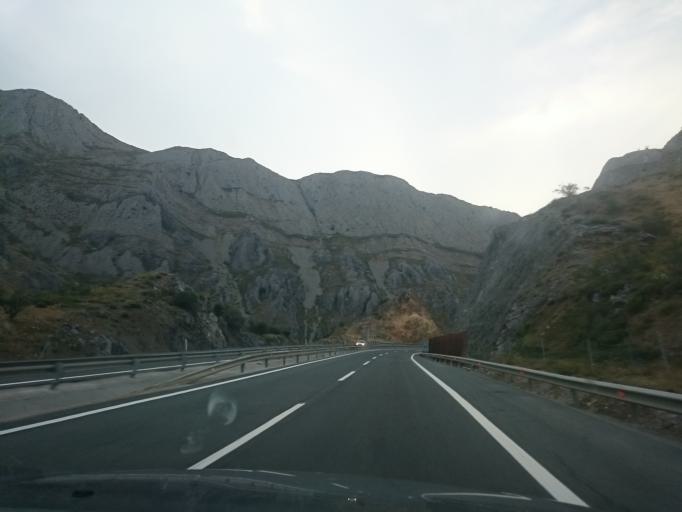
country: ES
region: Castille and Leon
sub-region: Provincia de Leon
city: Sena de Luna
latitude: 42.9318
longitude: -5.8515
